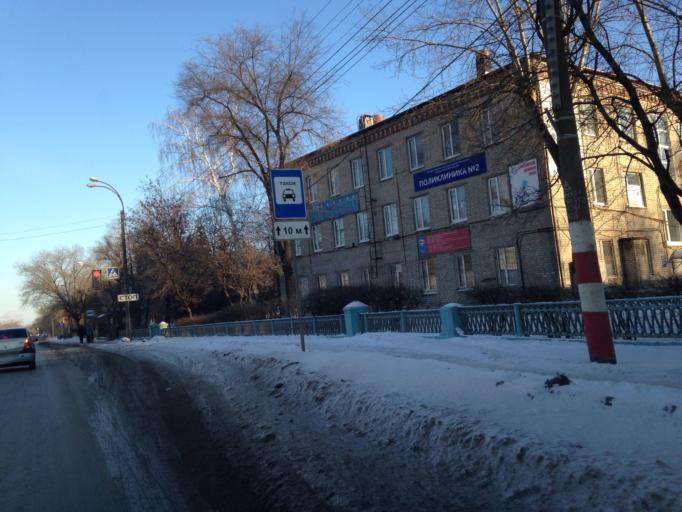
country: RU
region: Ulyanovsk
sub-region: Ulyanovskiy Rayon
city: Ulyanovsk
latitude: 54.2876
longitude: 48.3629
